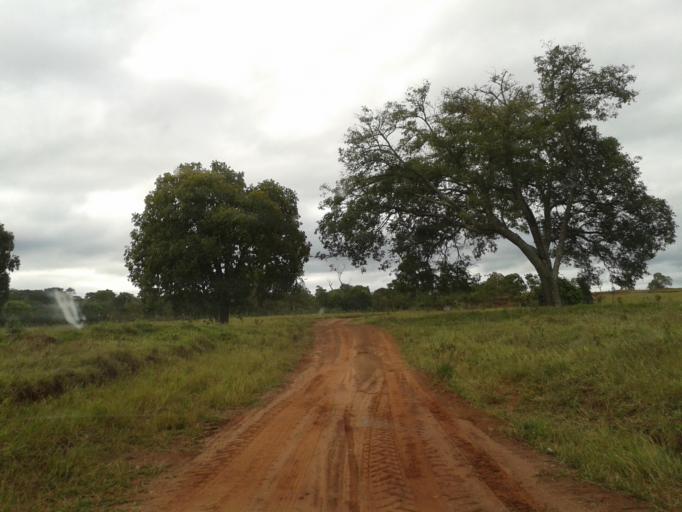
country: BR
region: Minas Gerais
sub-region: Campina Verde
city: Campina Verde
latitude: -19.4870
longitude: -49.6538
